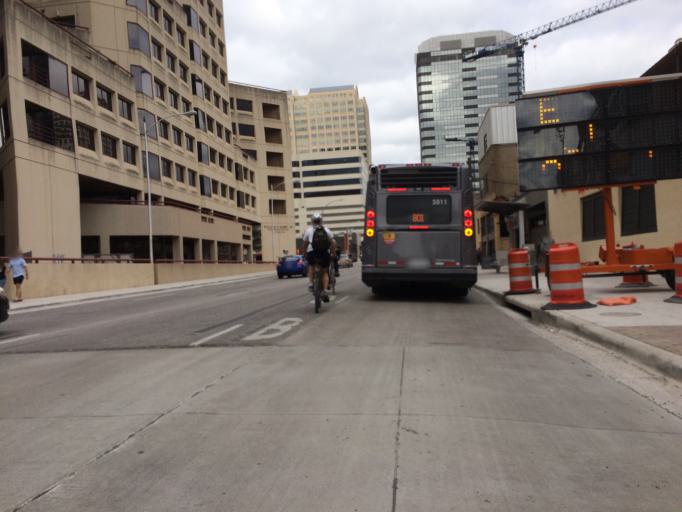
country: US
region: Texas
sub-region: Travis County
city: Austin
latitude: 30.2660
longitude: -97.7462
